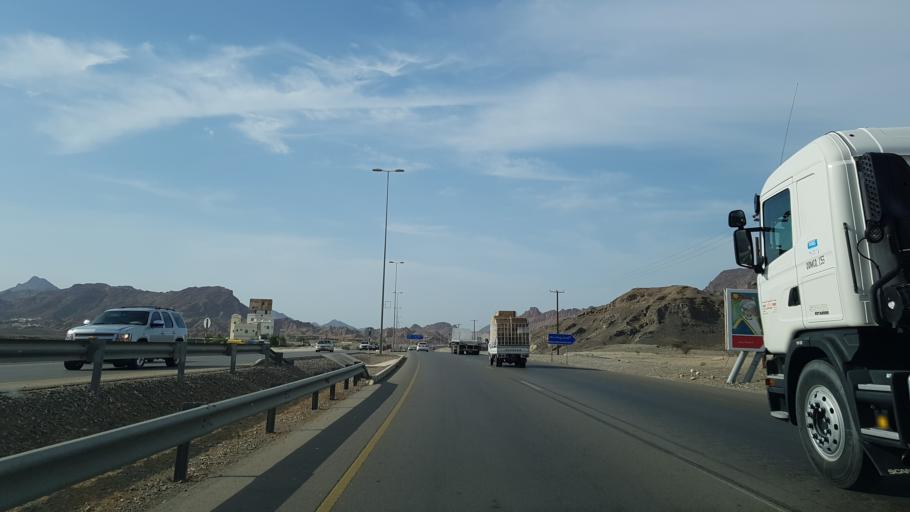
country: OM
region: Muhafazat ad Dakhiliyah
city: Bidbid
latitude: 23.4254
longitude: 58.1214
